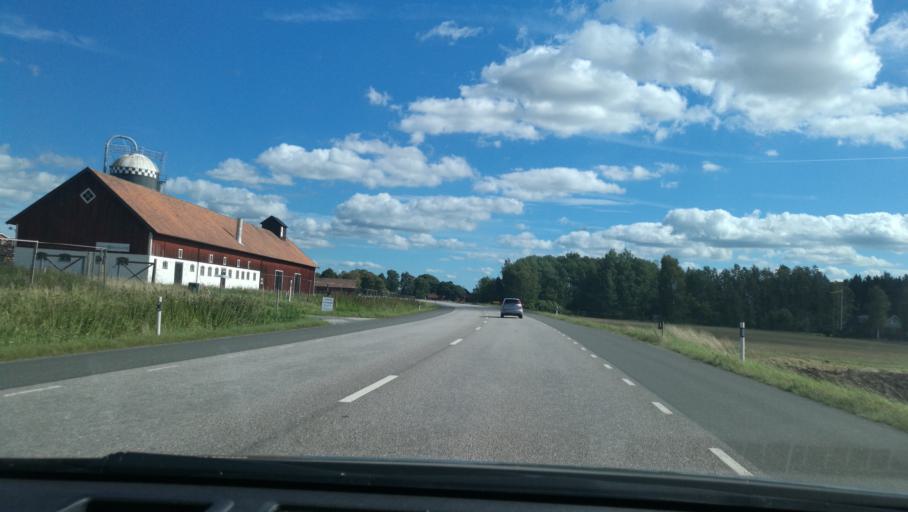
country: SE
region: Vaestra Goetaland
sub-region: Gotene Kommun
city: Kallby
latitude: 58.5086
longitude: 13.3841
